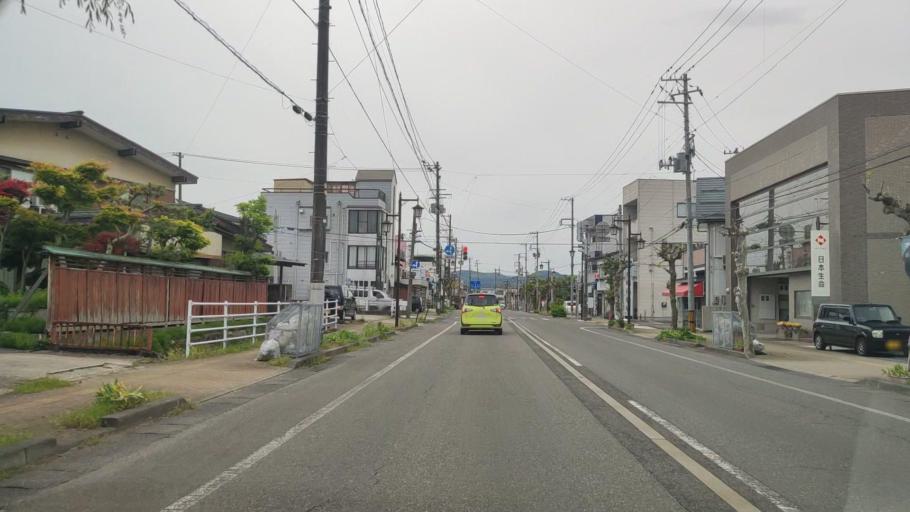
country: JP
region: Niigata
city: Gosen
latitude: 37.7377
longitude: 139.1790
